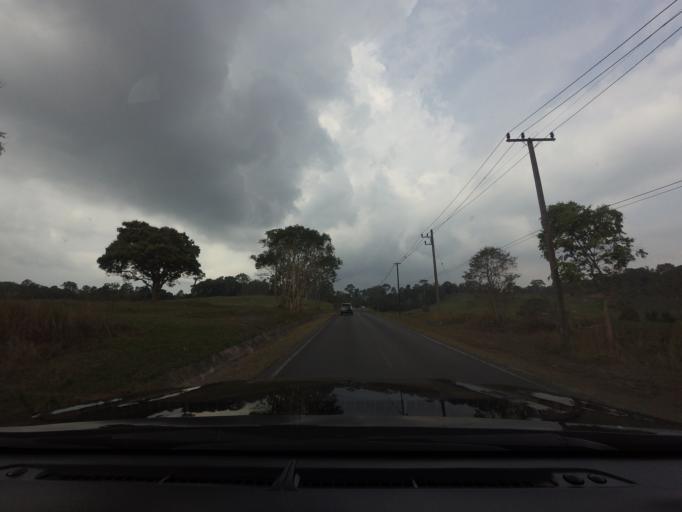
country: TH
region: Nakhon Nayok
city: Nakhon Nayok
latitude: 14.4176
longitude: 101.3704
